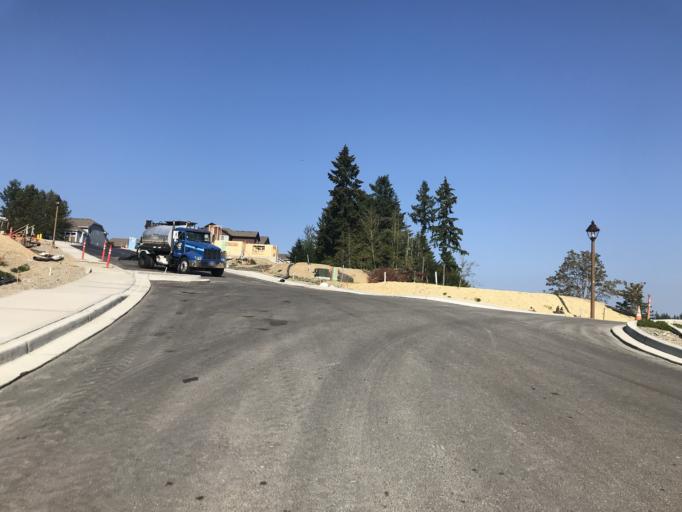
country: US
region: Washington
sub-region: Kitsap County
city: Poulsbo
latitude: 47.7253
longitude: -122.6245
